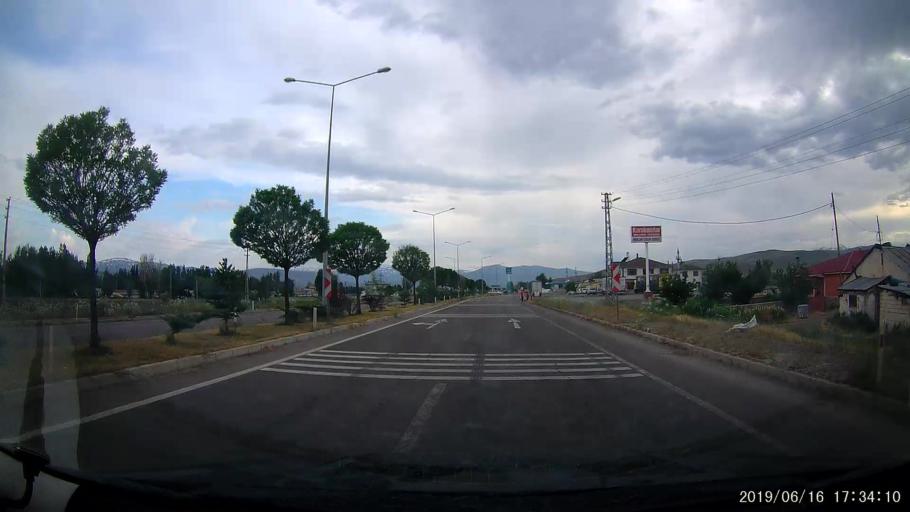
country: TR
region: Erzincan
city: Tercan
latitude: 39.7438
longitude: 40.2712
